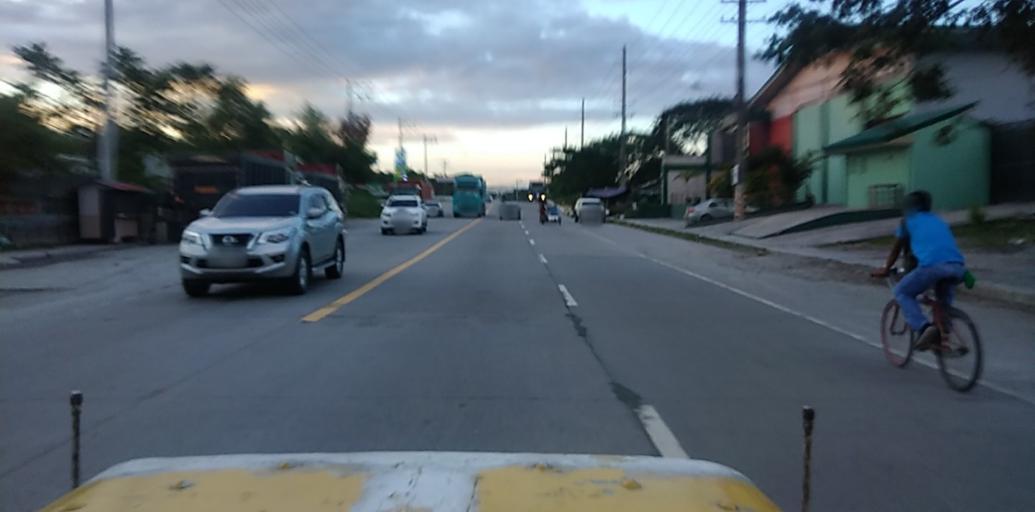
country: PH
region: Central Luzon
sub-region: Province of Pampanga
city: Calibutbut
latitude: 15.1172
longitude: 120.5929
